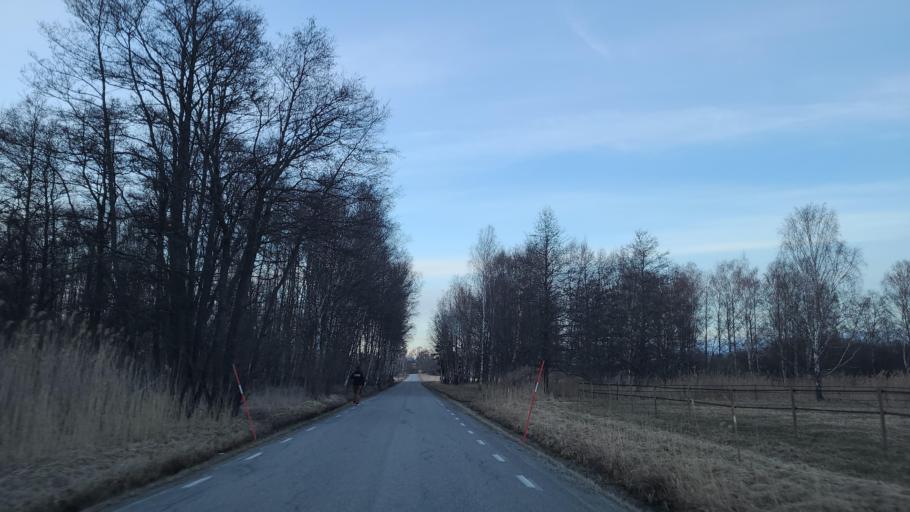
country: SE
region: Stockholm
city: Stenhamra
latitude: 59.4123
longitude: 17.6631
